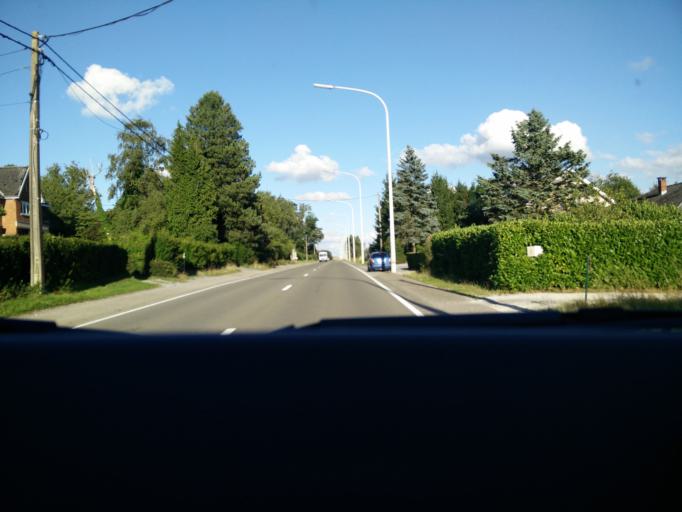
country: BE
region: Wallonia
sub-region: Province du Hainaut
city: Beaumont
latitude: 50.2377
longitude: 4.2496
